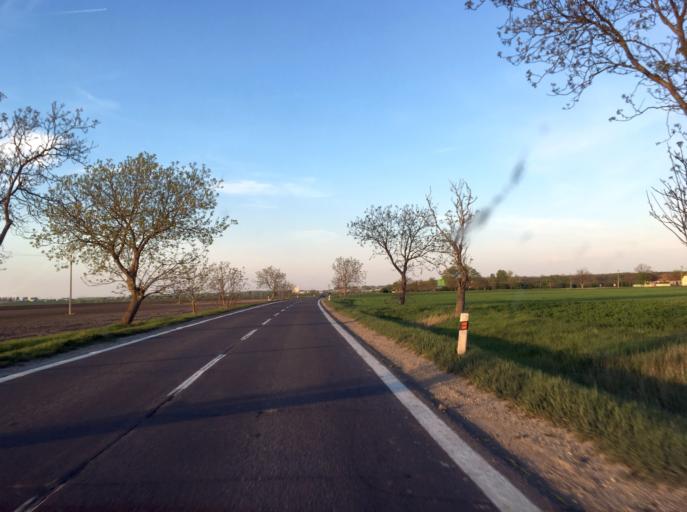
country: SK
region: Trnavsky
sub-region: Okres Dunajska Streda
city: Velky Meder
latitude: 47.8527
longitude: 17.7388
